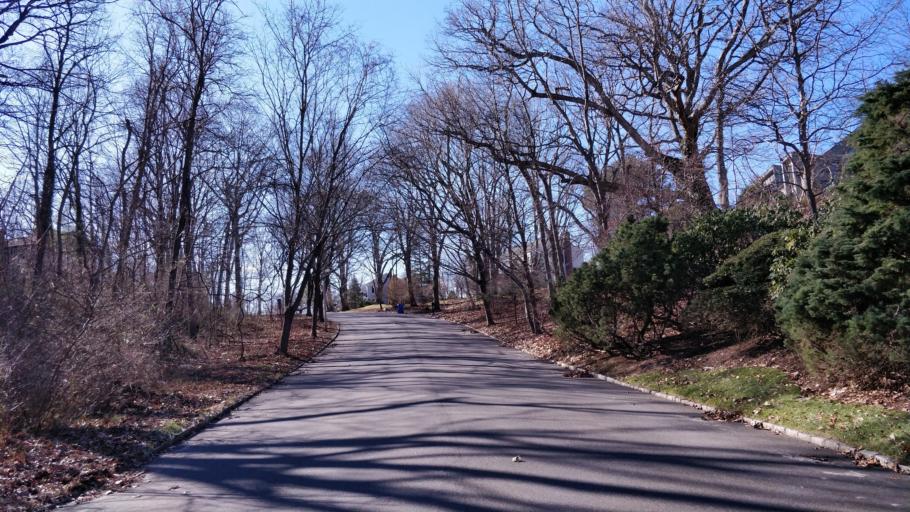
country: US
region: New York
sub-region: Suffolk County
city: Mount Sinai
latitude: 40.9616
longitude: -73.0464
